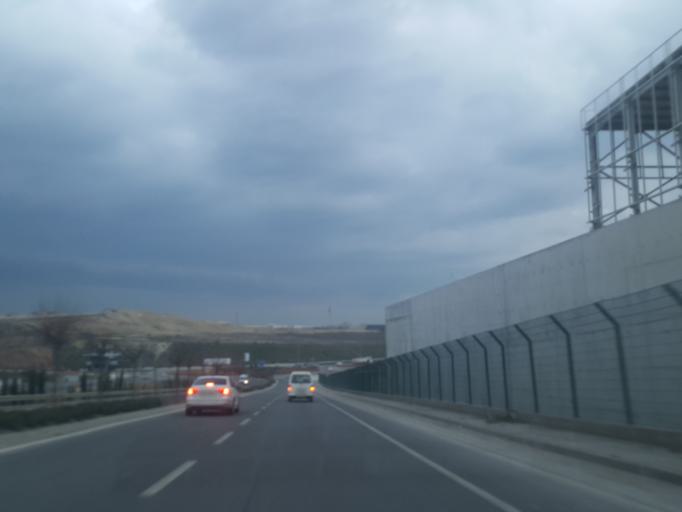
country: TR
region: Kocaeli
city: Tavsanli
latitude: 40.8252
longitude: 29.5596
